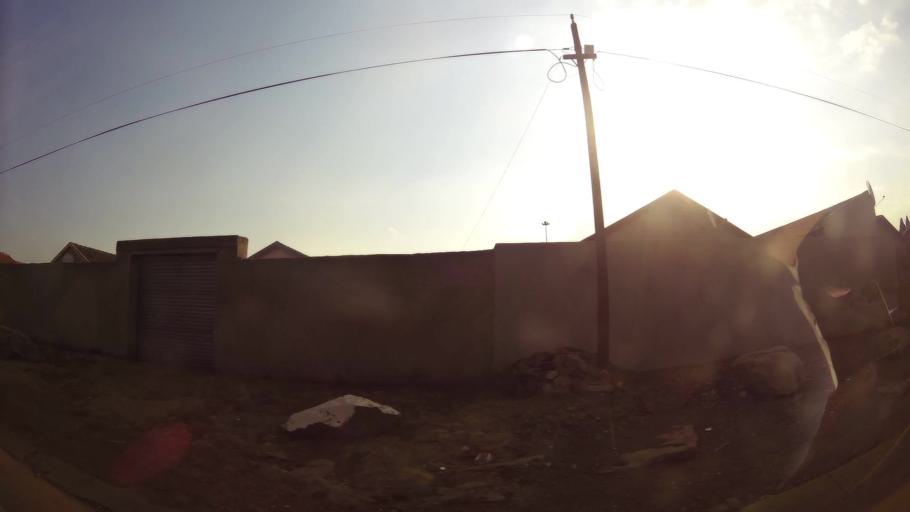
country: ZA
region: Gauteng
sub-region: Ekurhuleni Metropolitan Municipality
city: Germiston
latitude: -26.3676
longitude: 28.2062
